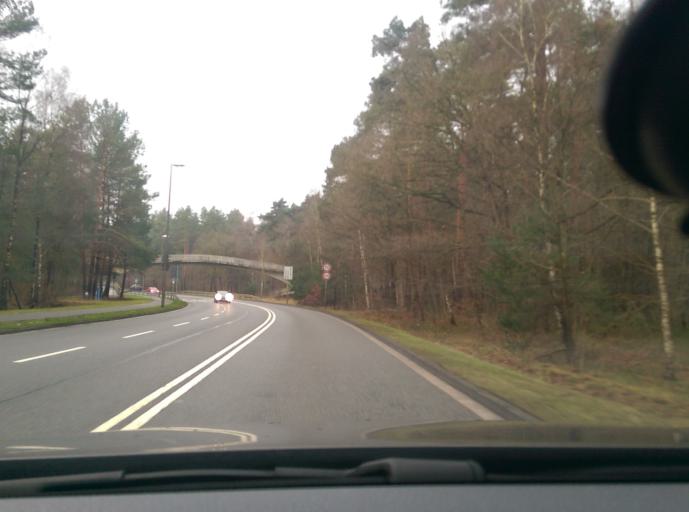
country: DE
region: Lower Saxony
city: Celle
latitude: 52.6155
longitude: 10.0376
